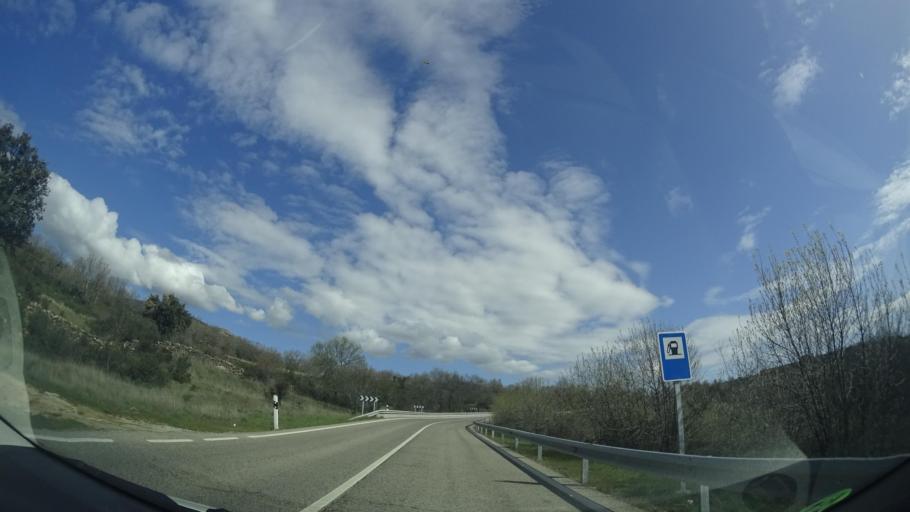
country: ES
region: Madrid
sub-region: Provincia de Madrid
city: Miraflores de la Sierra
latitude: 40.7736
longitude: -3.7789
